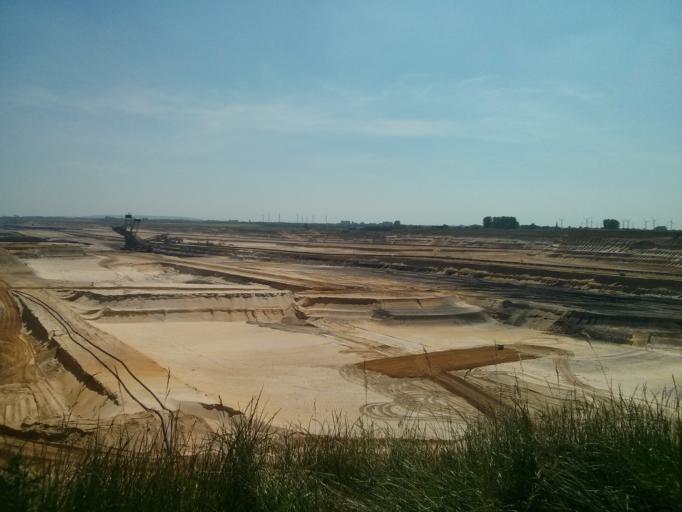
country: DE
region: North Rhine-Westphalia
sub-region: Regierungsbezirk Dusseldorf
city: Juchen
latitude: 51.0929
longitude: 6.4473
